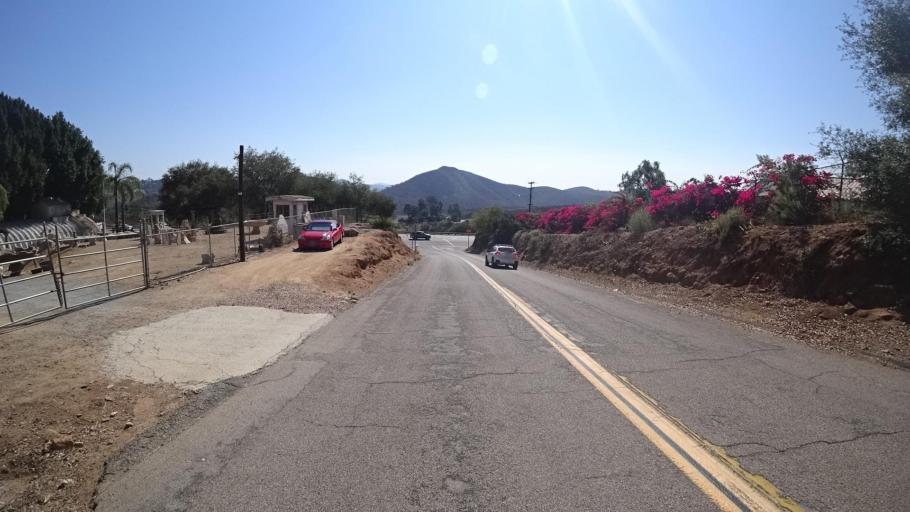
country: US
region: California
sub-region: San Diego County
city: Escondido
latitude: 33.0628
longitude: -117.1250
